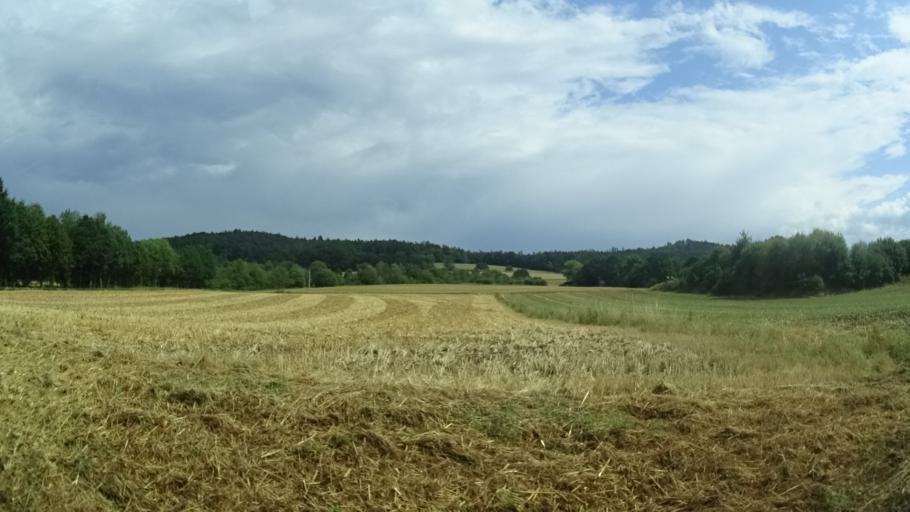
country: DE
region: Hesse
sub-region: Regierungsbezirk Kassel
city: Niederaula
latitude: 50.7719
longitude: 9.5978
